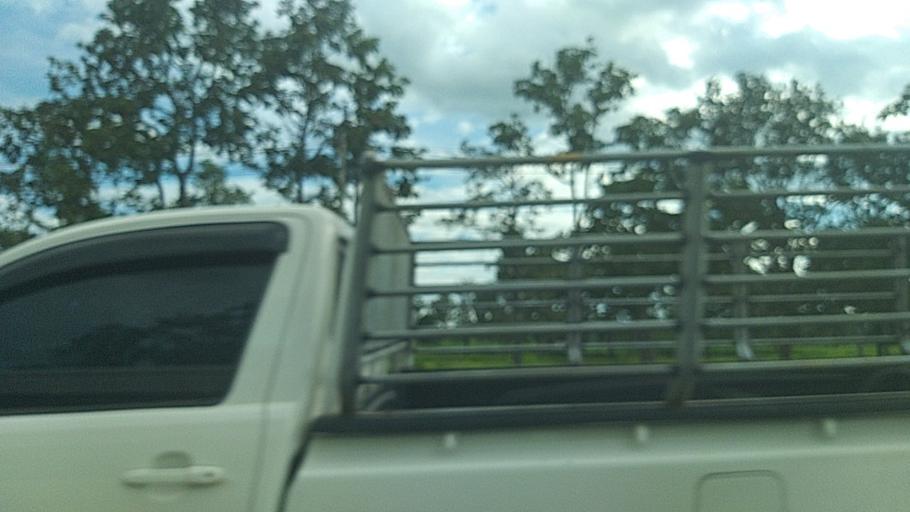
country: TH
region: Surin
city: Kap Choeng
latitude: 14.5436
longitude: 103.5170
